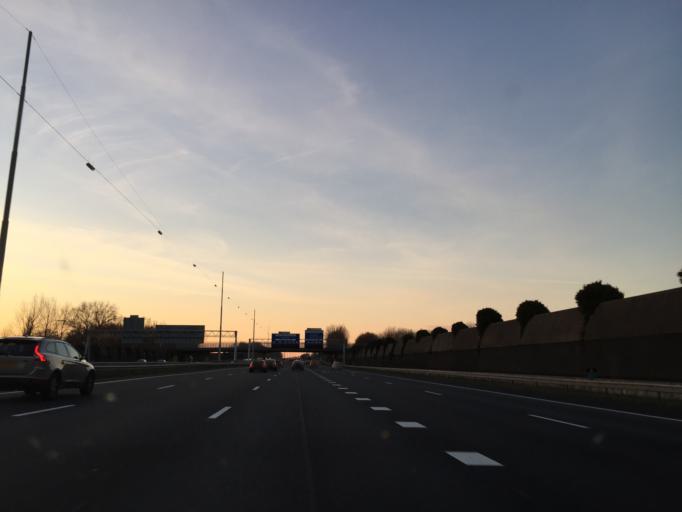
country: NL
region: South Holland
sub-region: Gemeente Ridderkerk
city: Ridderkerk
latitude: 51.8457
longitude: 4.6085
